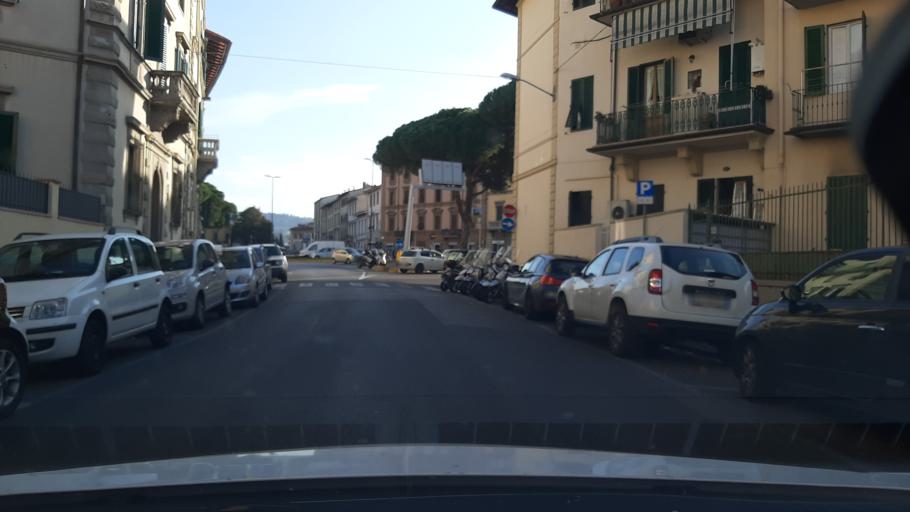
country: IT
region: Tuscany
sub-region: Province of Florence
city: Fiesole
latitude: 43.7742
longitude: 11.2855
